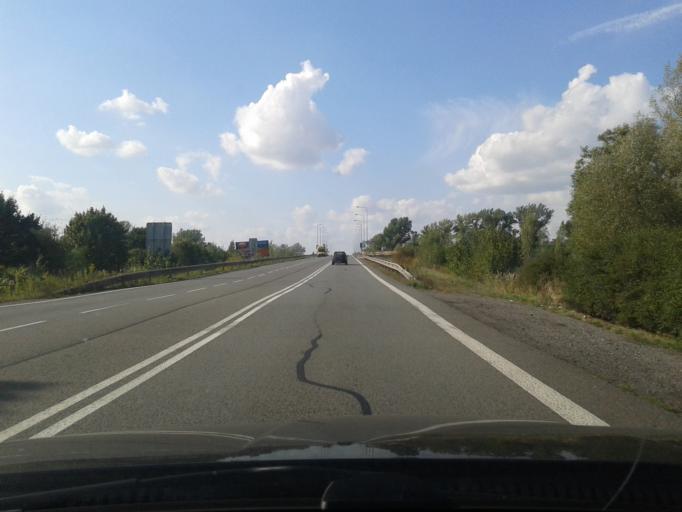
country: CZ
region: Moravskoslezsky
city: Stary Bohumin
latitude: 49.9142
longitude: 18.3270
